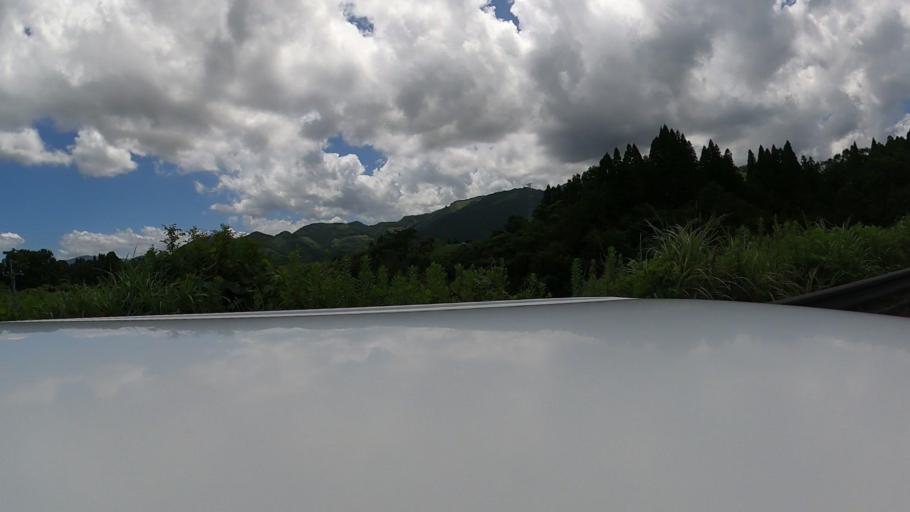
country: JP
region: Miyazaki
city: Nobeoka
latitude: 32.5867
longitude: 131.5108
